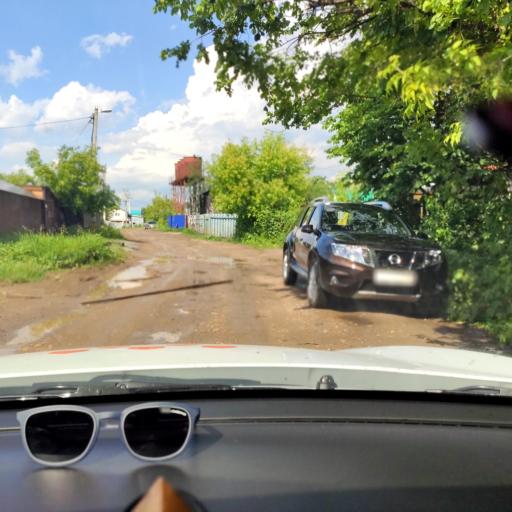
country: RU
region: Tatarstan
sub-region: Zelenodol'skiy Rayon
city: Vasil'yevo
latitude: 55.8247
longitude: 48.7249
